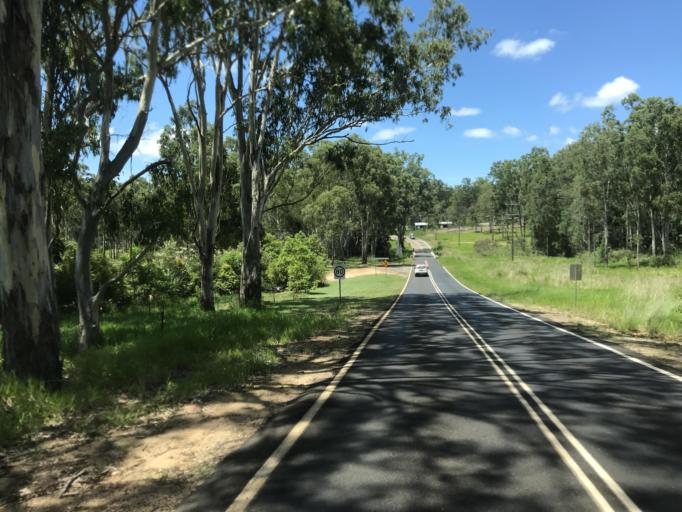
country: AU
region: Queensland
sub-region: Tablelands
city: Atherton
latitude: -17.4146
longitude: 145.3927
